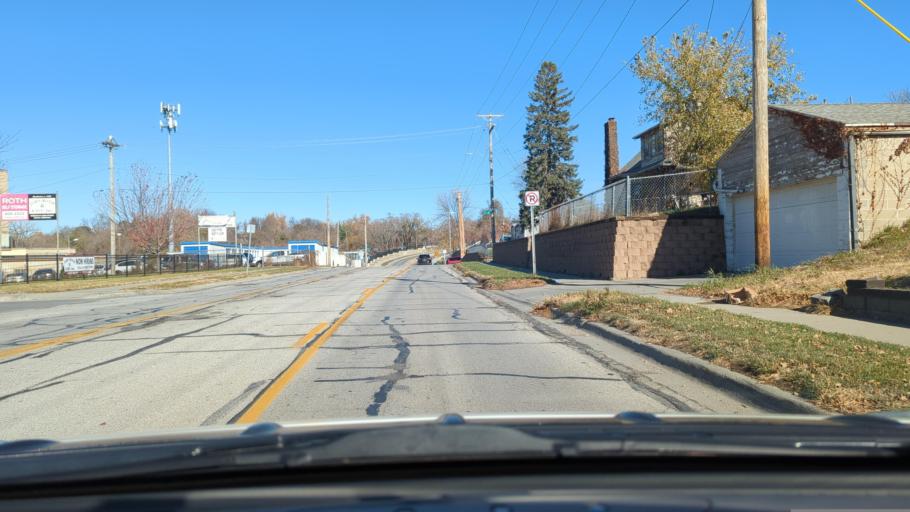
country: US
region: Nebraska
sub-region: Sarpy County
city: La Vista
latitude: 41.2030
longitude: -95.9770
